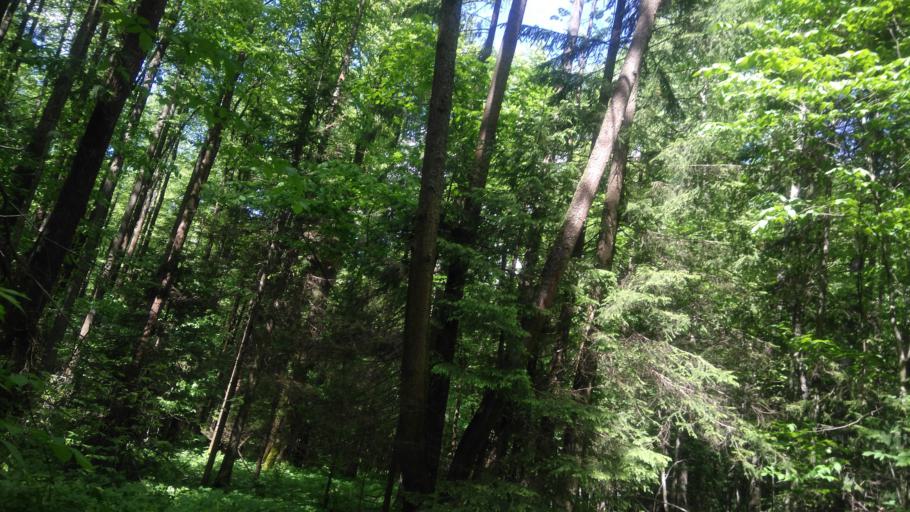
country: RU
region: Perm
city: Ferma
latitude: 57.9671
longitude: 56.3368
